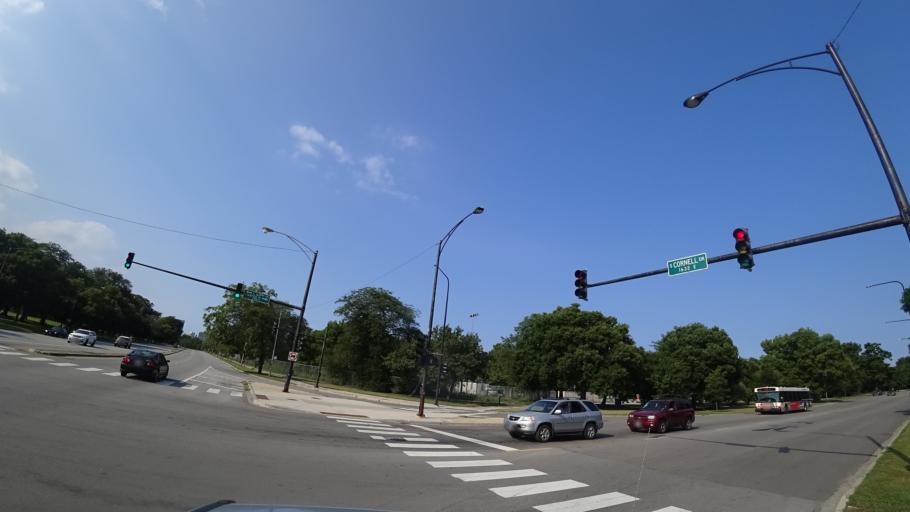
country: US
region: Illinois
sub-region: Cook County
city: Chicago
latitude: 41.7806
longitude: -87.5843
